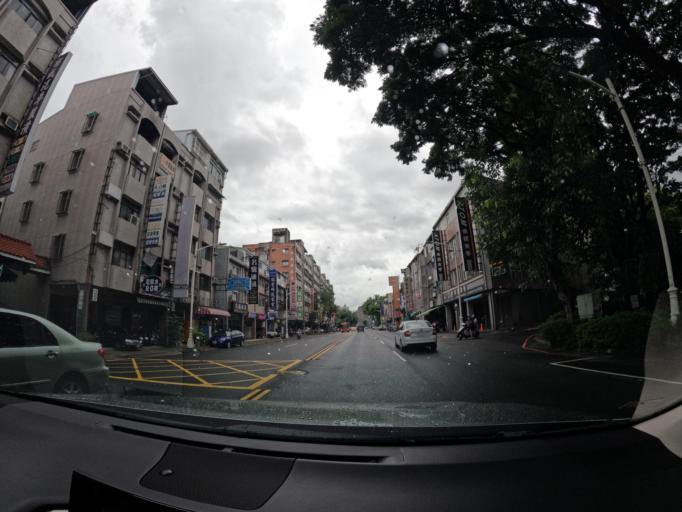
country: TW
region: Kaohsiung
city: Kaohsiung
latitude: 22.6341
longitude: 120.3183
